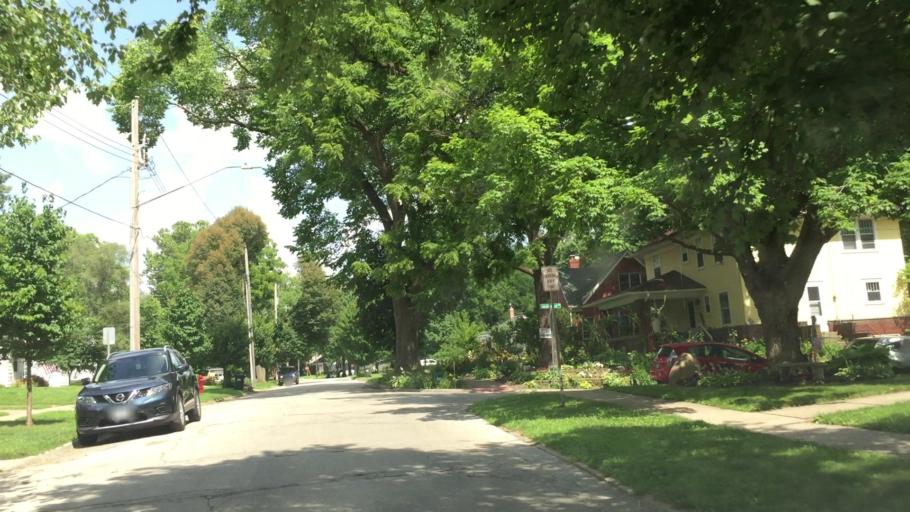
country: US
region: Iowa
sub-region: Johnson County
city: Iowa City
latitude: 41.6588
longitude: -91.5146
